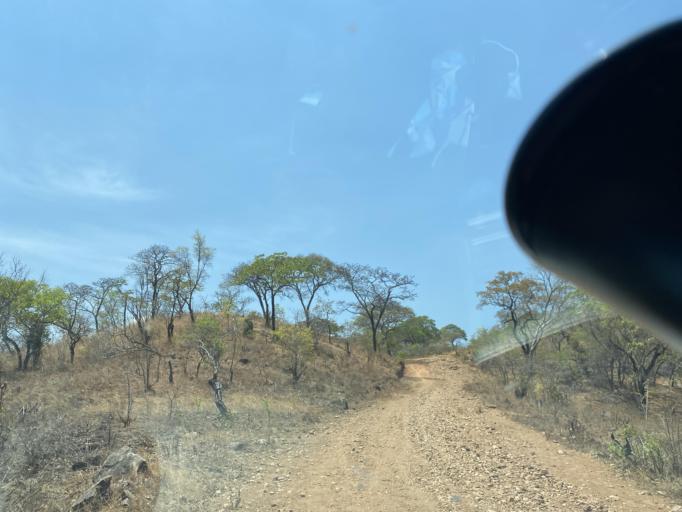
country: ZM
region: Lusaka
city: Kafue
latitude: -15.8063
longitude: 28.4397
